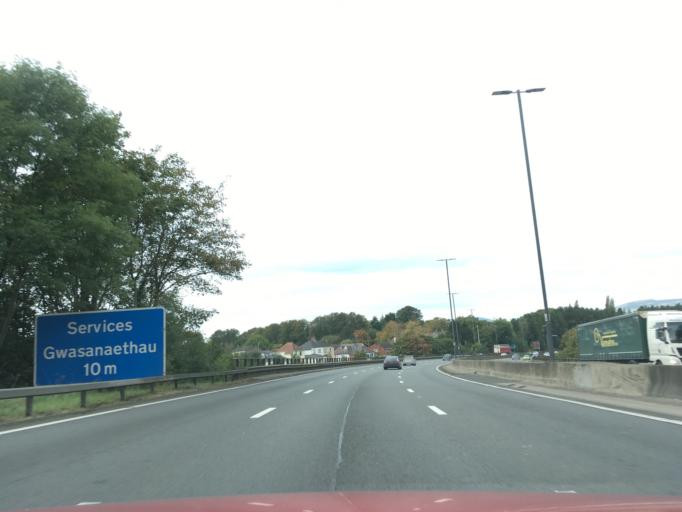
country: GB
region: Wales
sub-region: Newport
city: Caerleon
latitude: 51.5940
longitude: -2.9573
